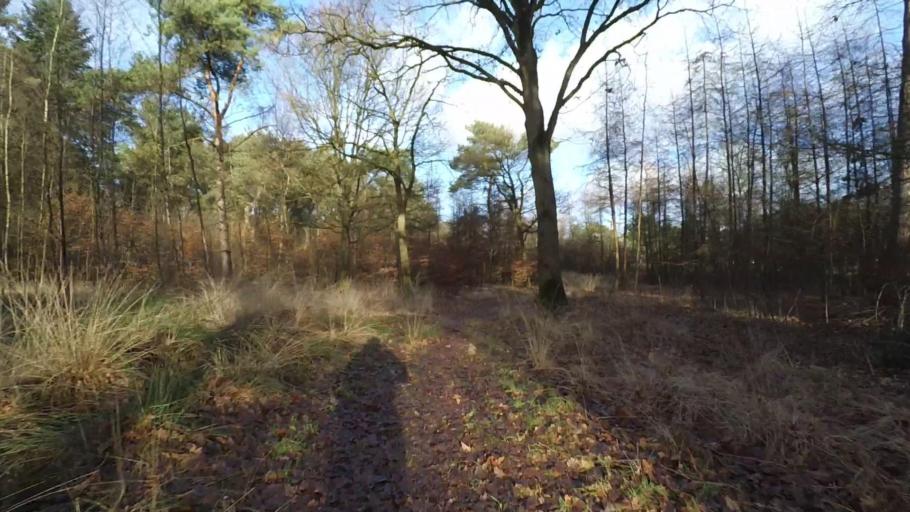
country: NL
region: Utrecht
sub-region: Gemeente Amersfoort
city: Amersfoort
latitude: 52.1145
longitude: 5.3666
